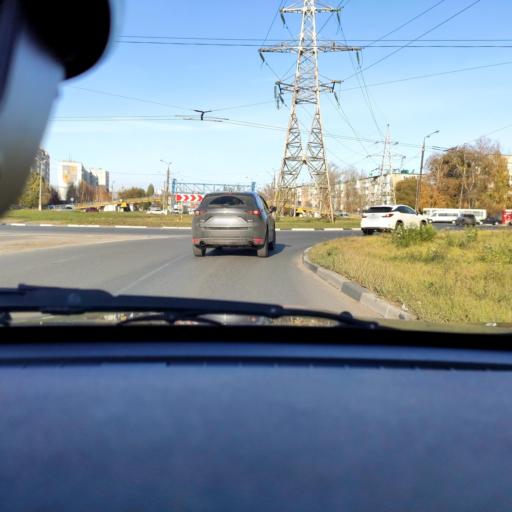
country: RU
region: Samara
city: Tol'yatti
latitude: 53.5284
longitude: 49.3965
